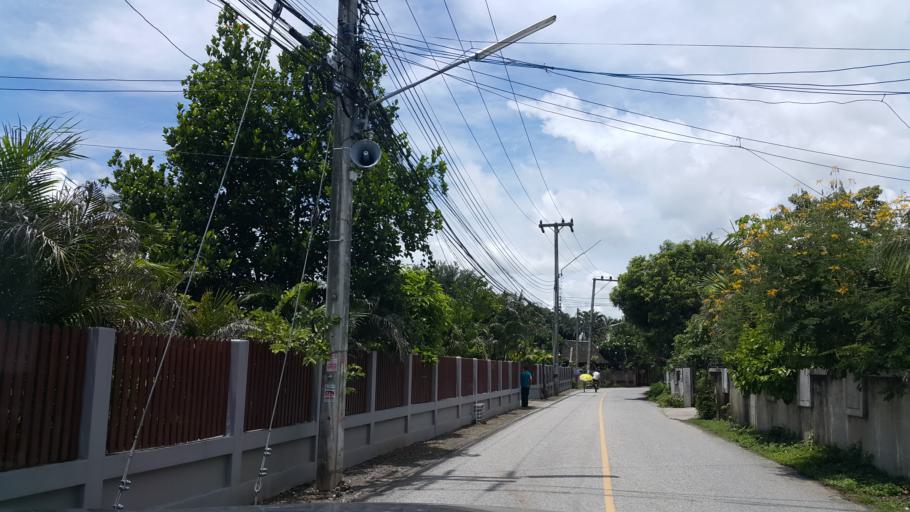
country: TH
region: Chiang Mai
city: San Kamphaeng
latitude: 18.7432
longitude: 99.1333
